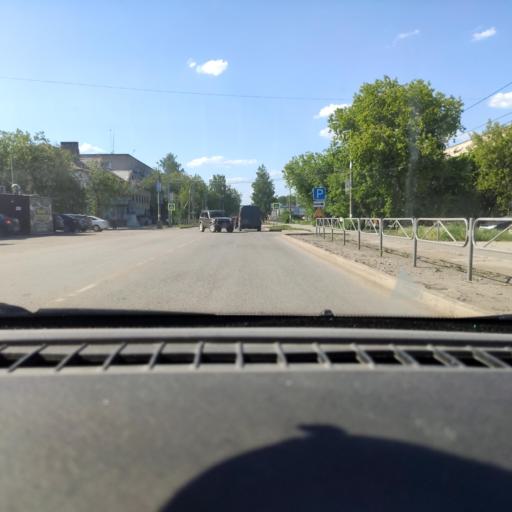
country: RU
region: Perm
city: Krasnokamsk
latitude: 58.0800
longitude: 55.7596
